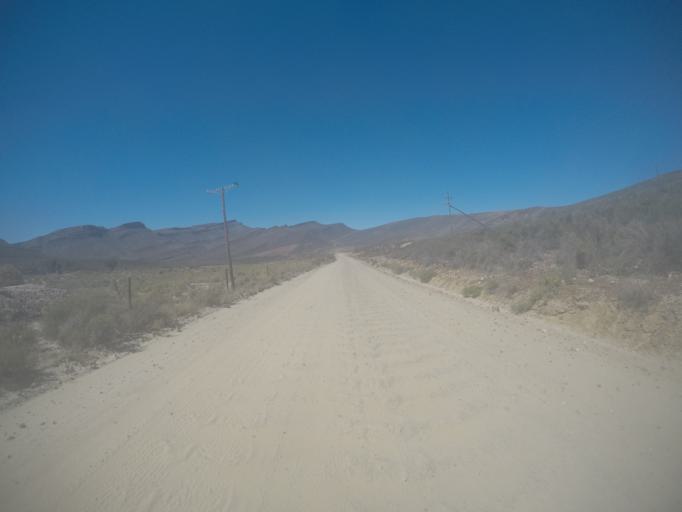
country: ZA
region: Western Cape
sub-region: West Coast District Municipality
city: Clanwilliam
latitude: -32.5531
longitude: 19.3612
